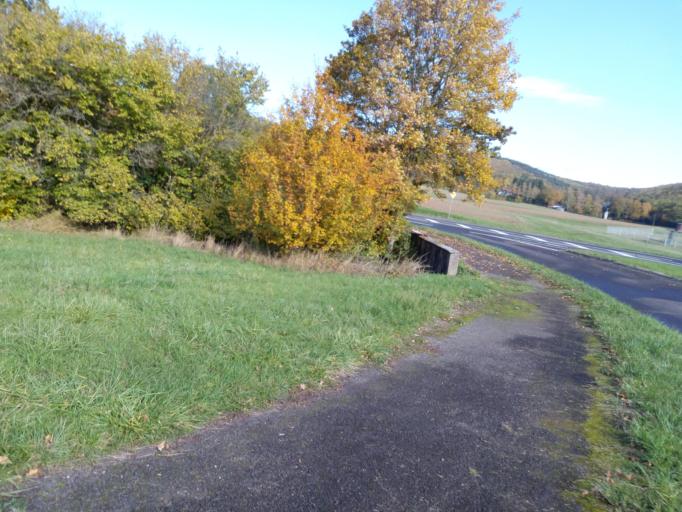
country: DE
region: Rheinland-Pfalz
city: Nussbaum
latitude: 49.8083
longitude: 7.6414
